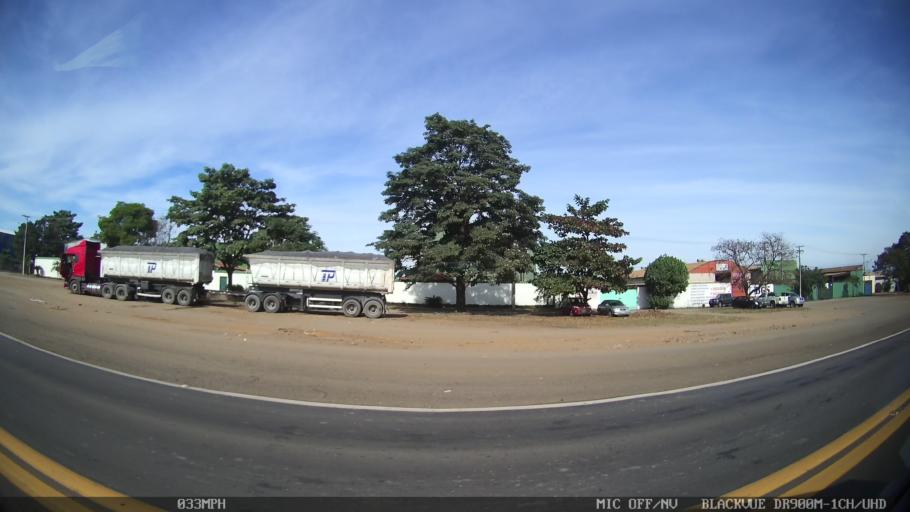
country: BR
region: Sao Paulo
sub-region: Rio Das Pedras
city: Rio das Pedras
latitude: -22.7945
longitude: -47.6167
